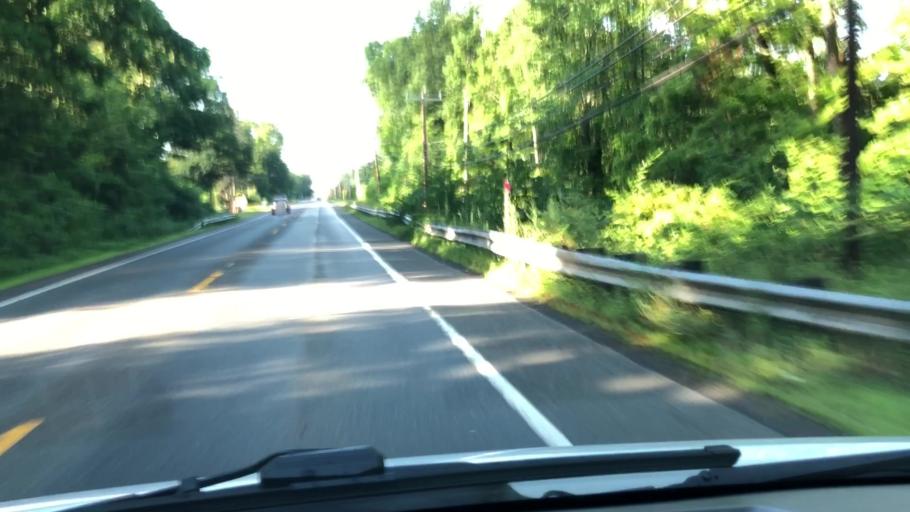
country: US
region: Massachusetts
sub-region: Franklin County
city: Greenfield
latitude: 42.5475
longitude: -72.6010
